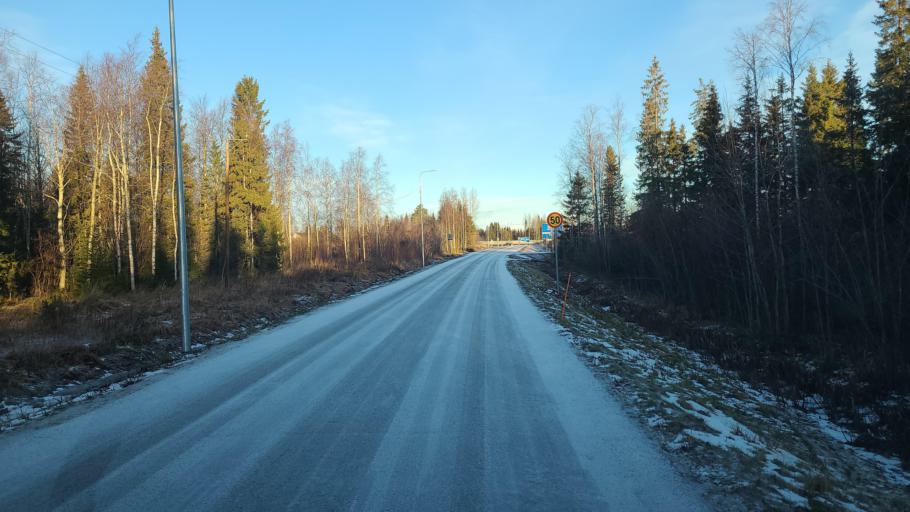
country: FI
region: Lapland
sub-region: Kemi-Tornio
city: Kemi
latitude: 65.6750
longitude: 24.7433
